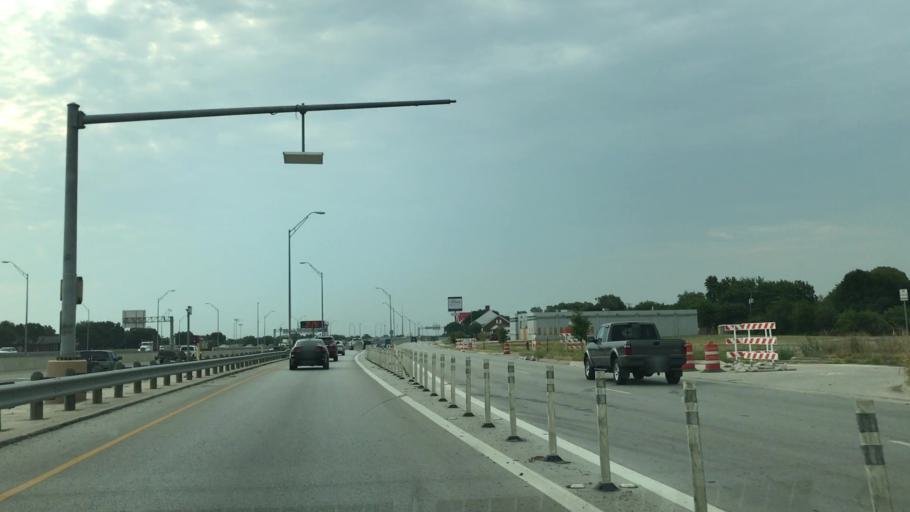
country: US
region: Texas
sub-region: Tarrant County
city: North Richland Hills
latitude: 32.8398
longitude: -97.2351
